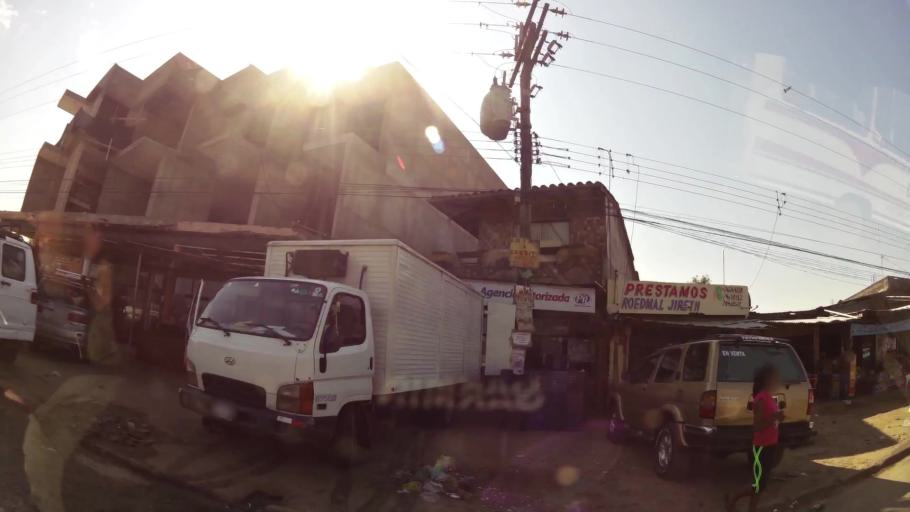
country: BO
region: Santa Cruz
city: Cotoca
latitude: -17.8172
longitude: -63.1167
